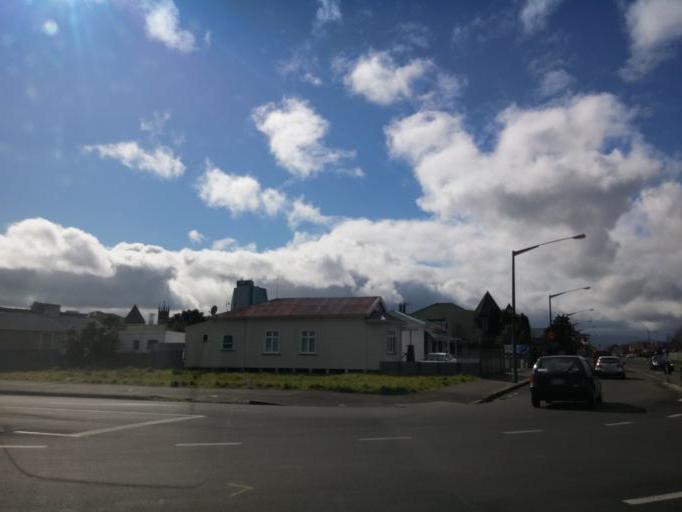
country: NZ
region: Manawatu-Wanganui
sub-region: Palmerston North City
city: Palmerston North
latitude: -40.3613
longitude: 175.6093
